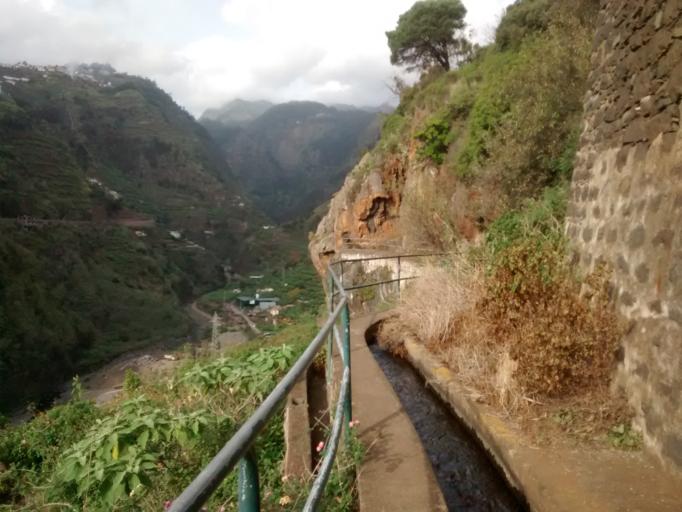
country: PT
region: Madeira
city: Camara de Lobos
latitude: 32.6582
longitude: -16.9609
